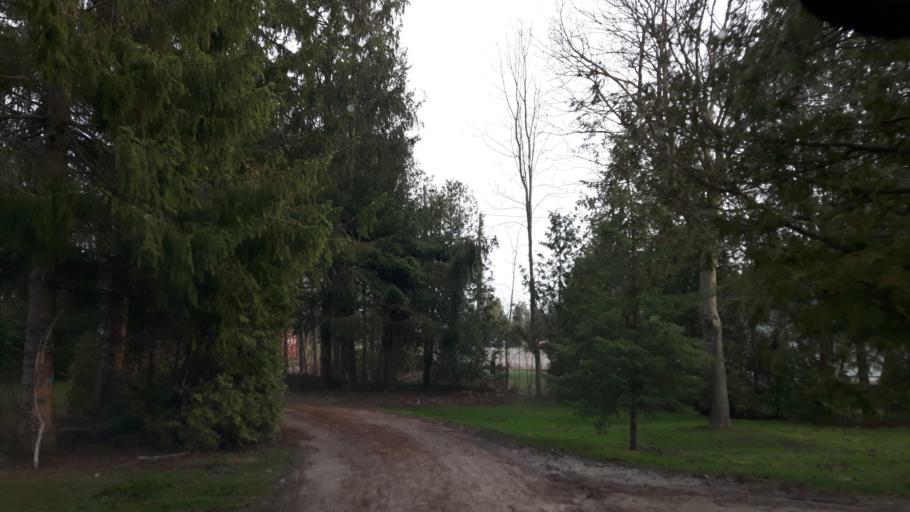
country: CA
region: Ontario
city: Bluewater
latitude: 43.5738
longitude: -81.7066
